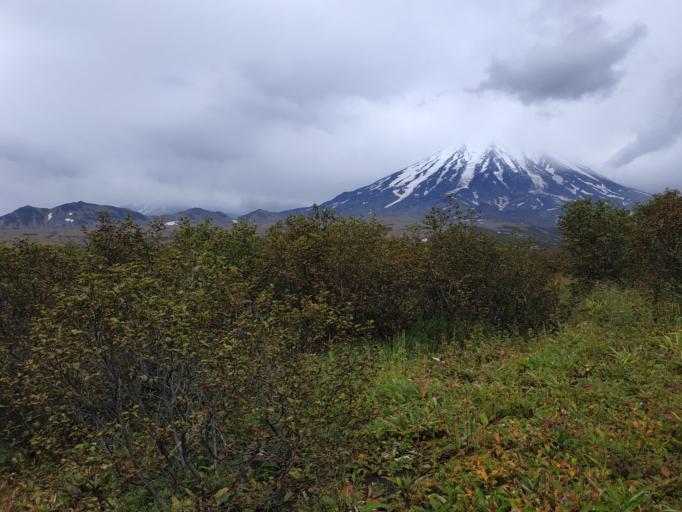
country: RU
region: Kamtsjatka
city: Petropavlovsk-Kamchatsky
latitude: 53.4101
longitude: 158.7475
